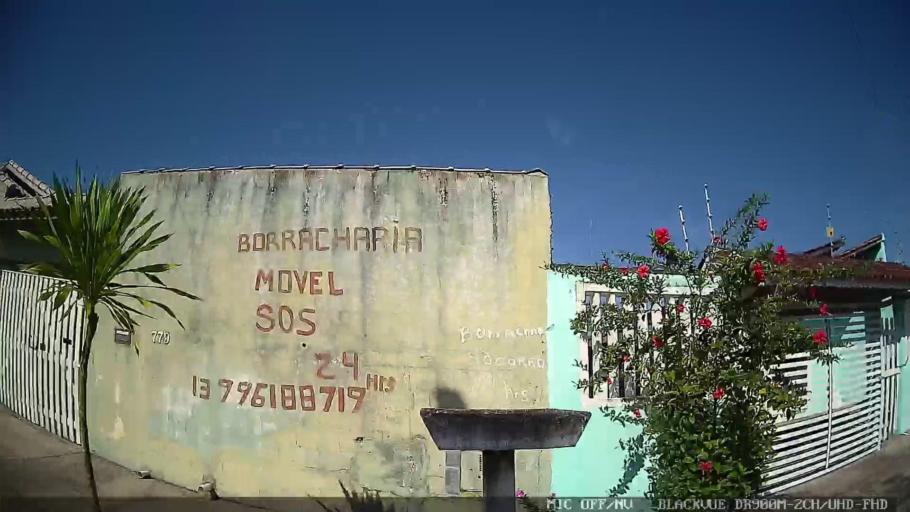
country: BR
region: Sao Paulo
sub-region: Peruibe
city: Peruibe
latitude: -24.2755
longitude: -46.9480
